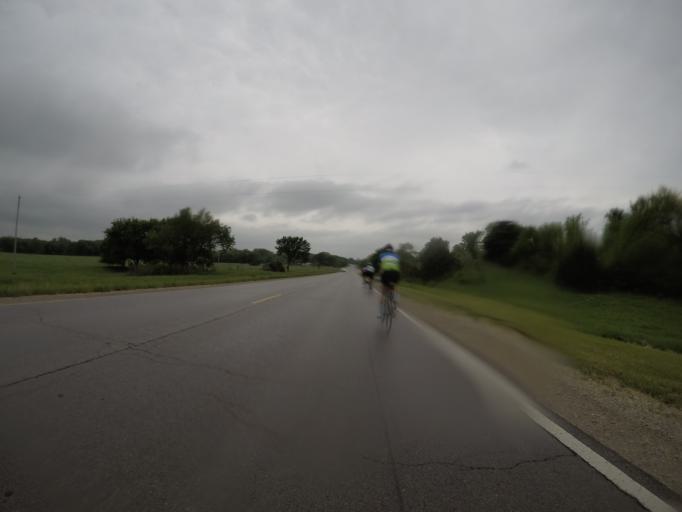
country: US
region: Kansas
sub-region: Pottawatomie County
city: Westmoreland
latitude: 39.4794
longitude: -96.1784
